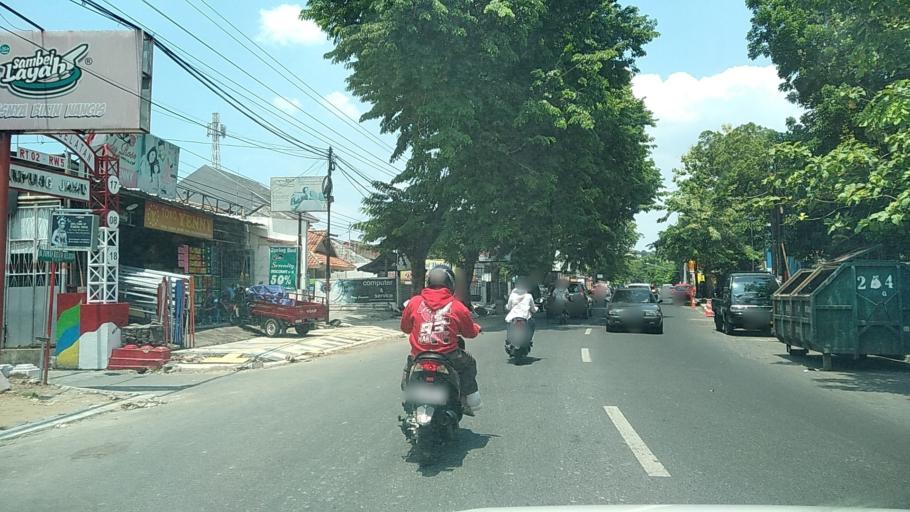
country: ID
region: Central Java
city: Semarang
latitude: -7.0050
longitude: 110.3969
